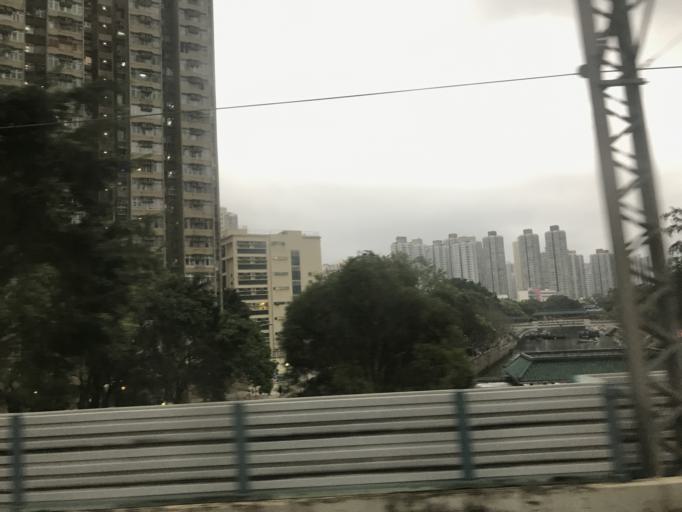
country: HK
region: Tai Po
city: Tai Po
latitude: 22.4496
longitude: 114.1624
